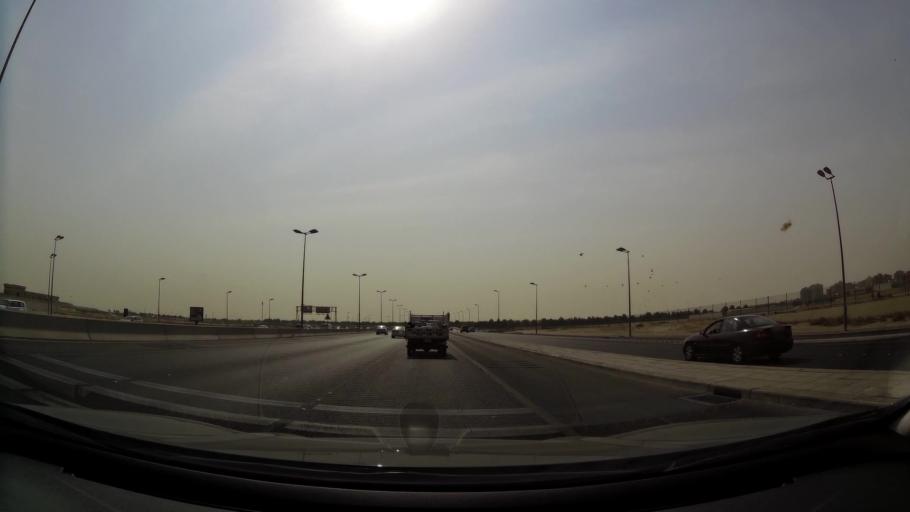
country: KW
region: Al Farwaniyah
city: Al Farwaniyah
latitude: 29.2634
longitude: 47.9525
